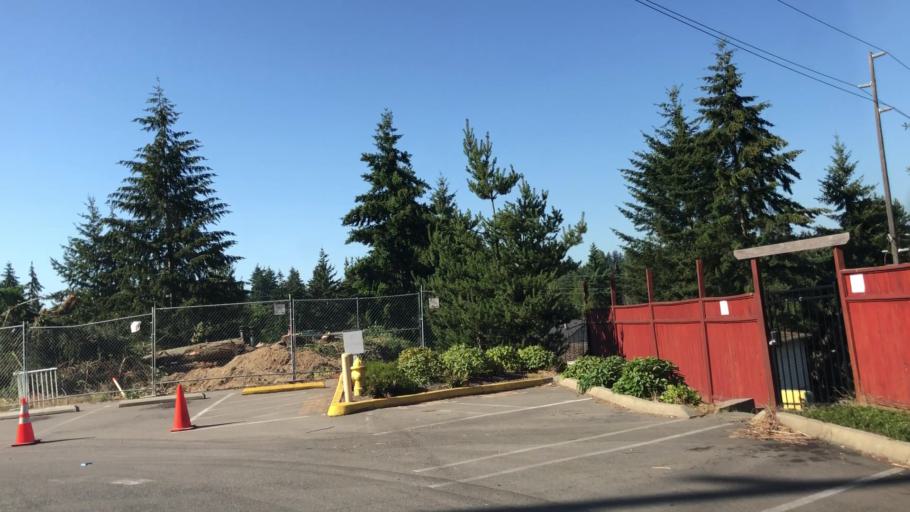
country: US
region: Washington
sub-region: Snohomish County
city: Mountlake Terrace
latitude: 47.7716
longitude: -122.3074
